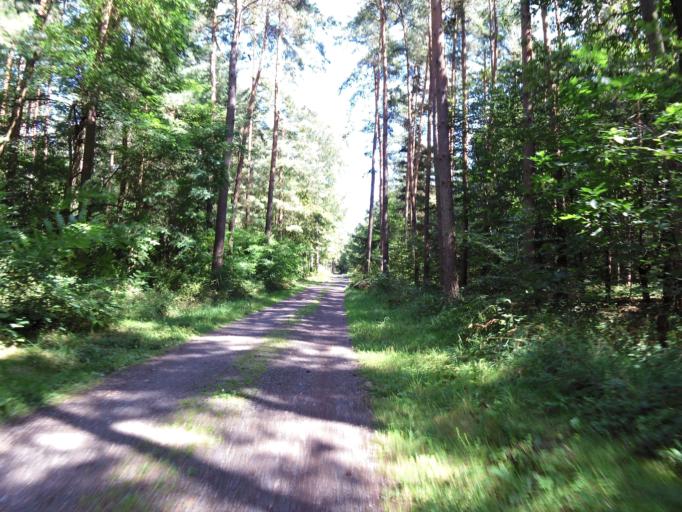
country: DE
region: Rheinland-Pfalz
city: Bellheim
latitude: 49.2112
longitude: 8.3004
